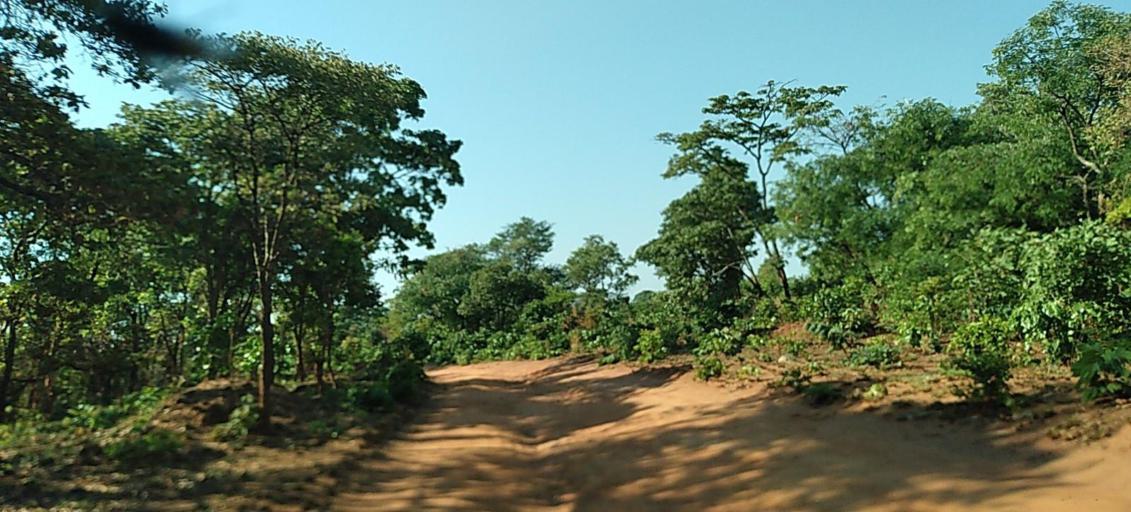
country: ZM
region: Central
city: Mkushi
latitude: -13.4691
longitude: 28.9164
